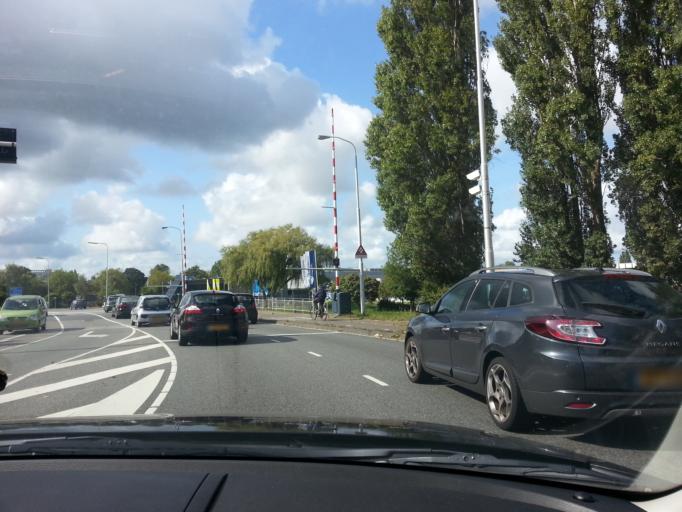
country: NL
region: South Holland
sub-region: Gemeente Leiden
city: Leiden
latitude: 52.1418
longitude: 4.4858
